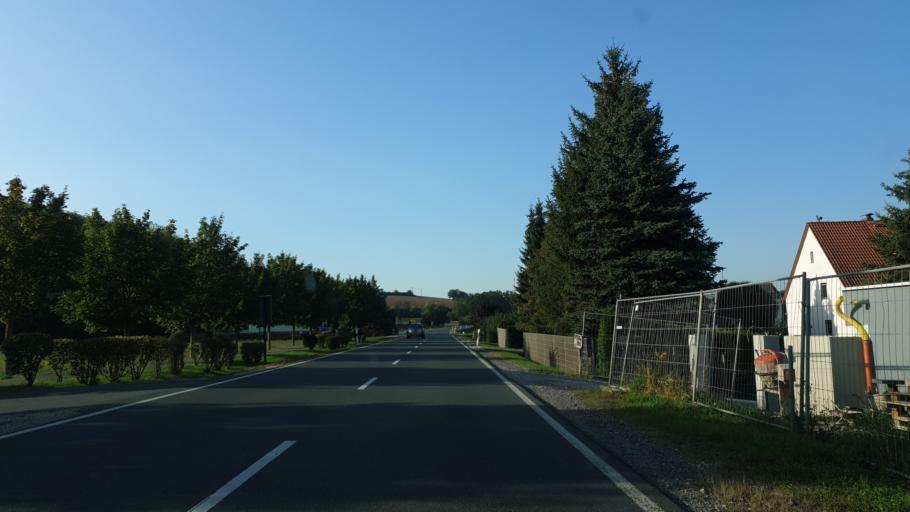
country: DE
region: Thuringia
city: Caaschwitz
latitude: 50.9490
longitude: 11.9878
